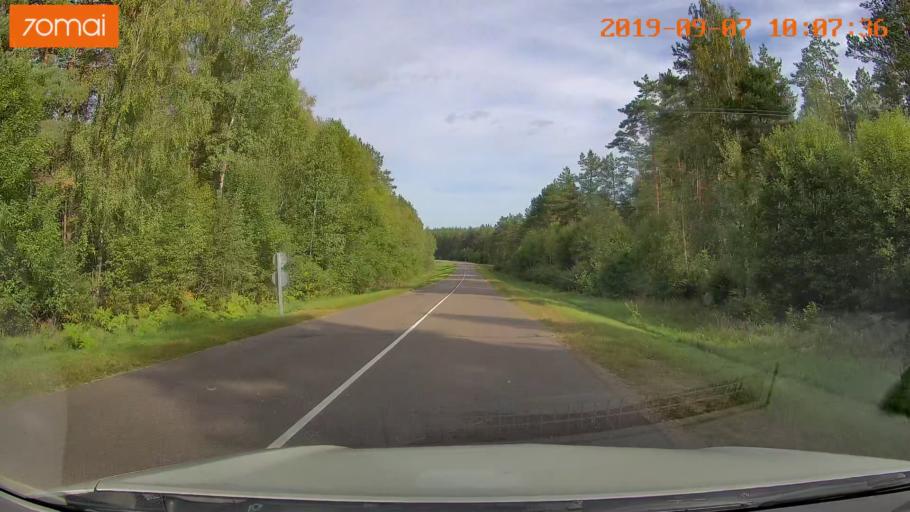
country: BY
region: Grodnenskaya
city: Voranava
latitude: 54.0776
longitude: 25.3960
